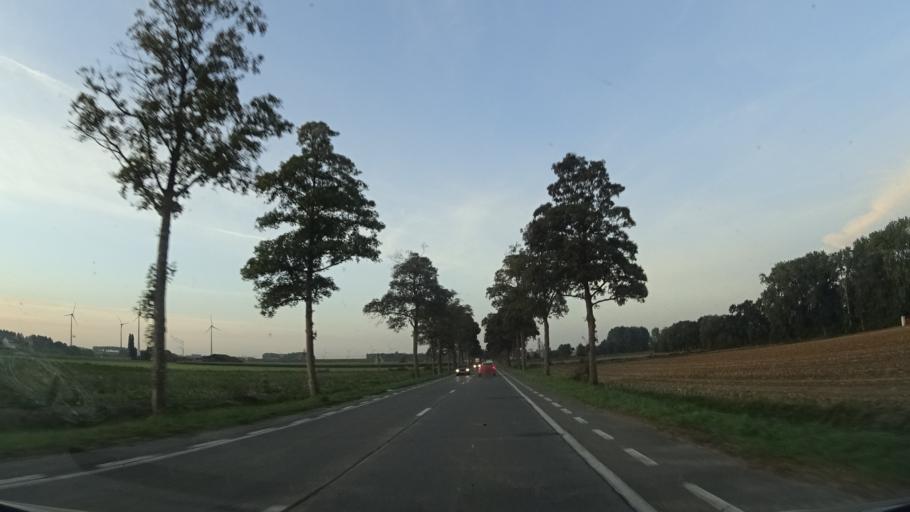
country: BE
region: Wallonia
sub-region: Province du Hainaut
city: Peruwelz
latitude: 50.5715
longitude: 3.6158
